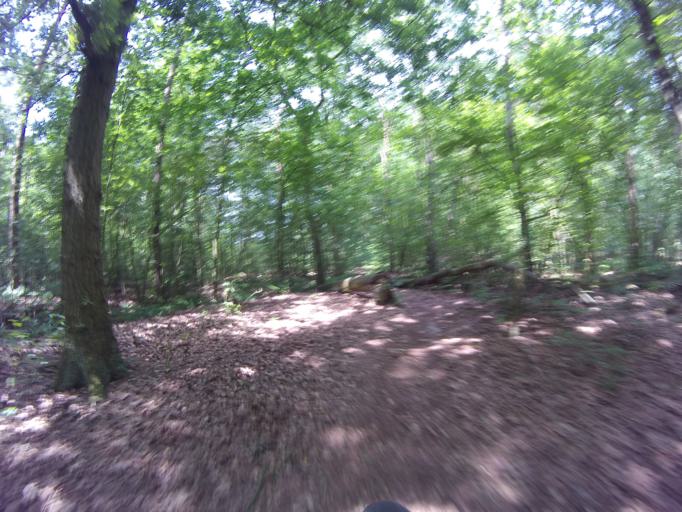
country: NL
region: Gelderland
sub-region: Gemeente Ede
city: Lunteren
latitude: 52.1028
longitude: 5.6438
